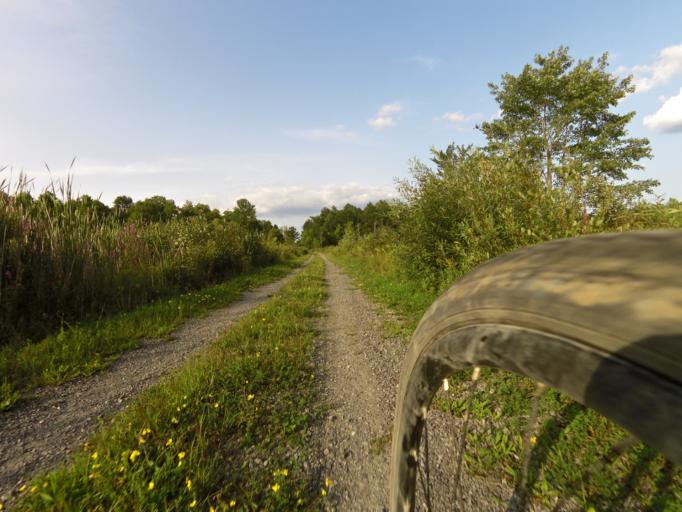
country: CA
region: Ontario
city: Kingston
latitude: 44.4887
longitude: -76.4553
